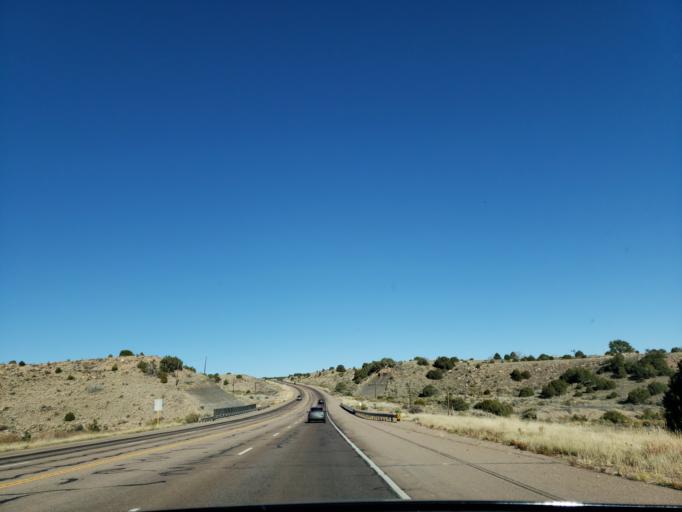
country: US
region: Colorado
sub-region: Fremont County
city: Penrose
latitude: 38.4686
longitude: -104.9912
